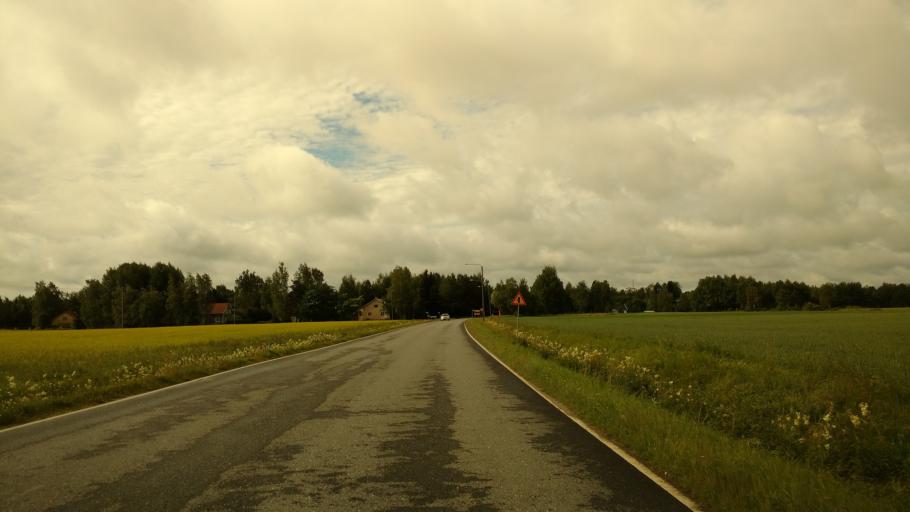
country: FI
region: Varsinais-Suomi
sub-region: Loimaa
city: Koski Tl
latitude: 60.6641
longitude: 23.1523
